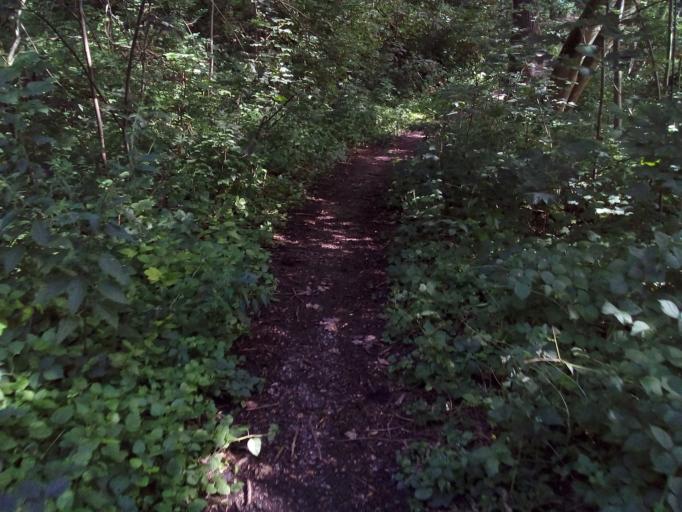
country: DE
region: Bavaria
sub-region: Upper Bavaria
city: Unterfoehring
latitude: 48.2042
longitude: 11.6469
